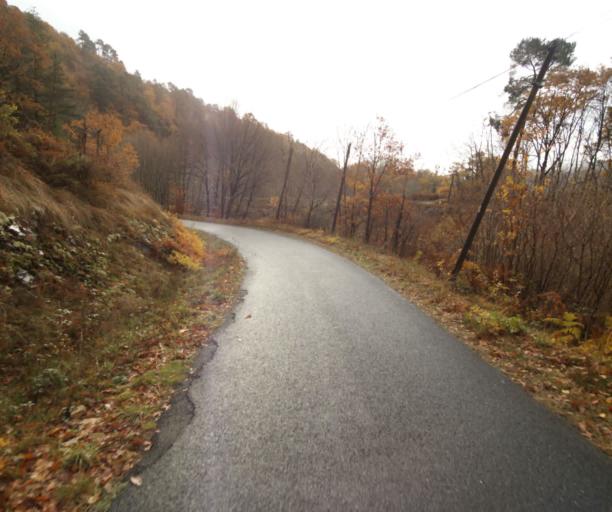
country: FR
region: Limousin
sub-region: Departement de la Correze
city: Cornil
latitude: 45.2035
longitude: 1.6599
